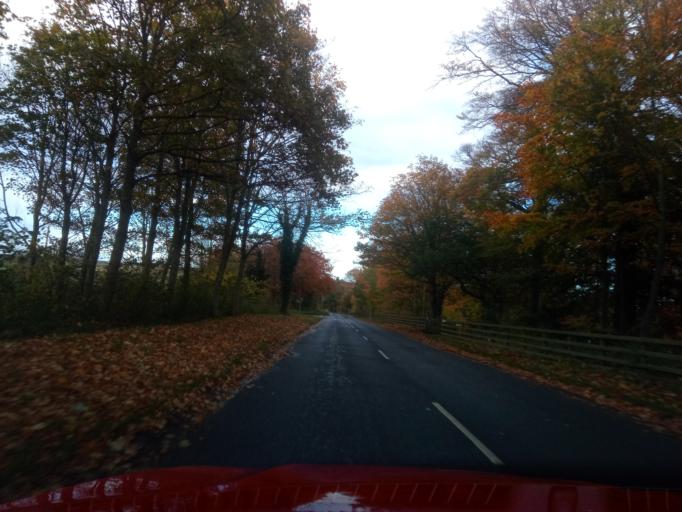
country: GB
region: England
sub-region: Northumberland
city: Ford
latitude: 55.6306
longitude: -2.0989
